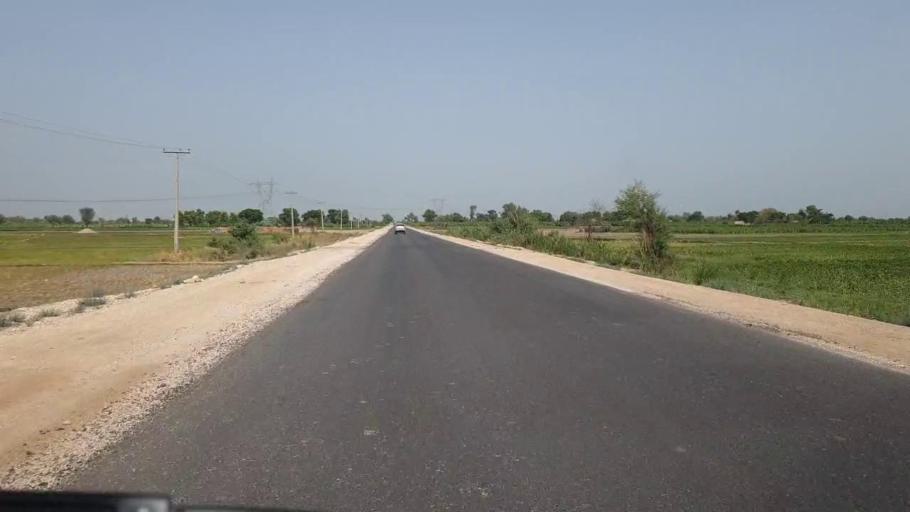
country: PK
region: Sindh
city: Sakrand
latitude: 26.2560
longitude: 68.1956
